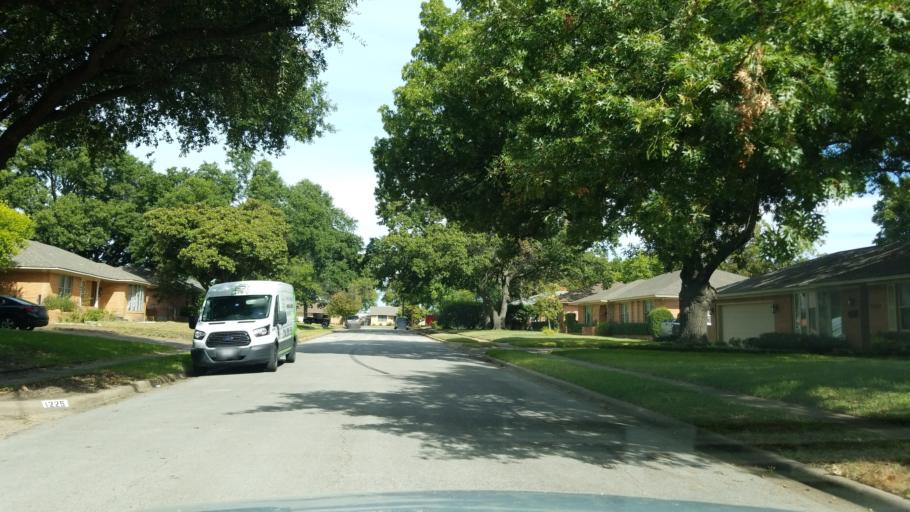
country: US
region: Texas
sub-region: Dallas County
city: Garland
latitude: 32.9023
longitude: -96.6619
